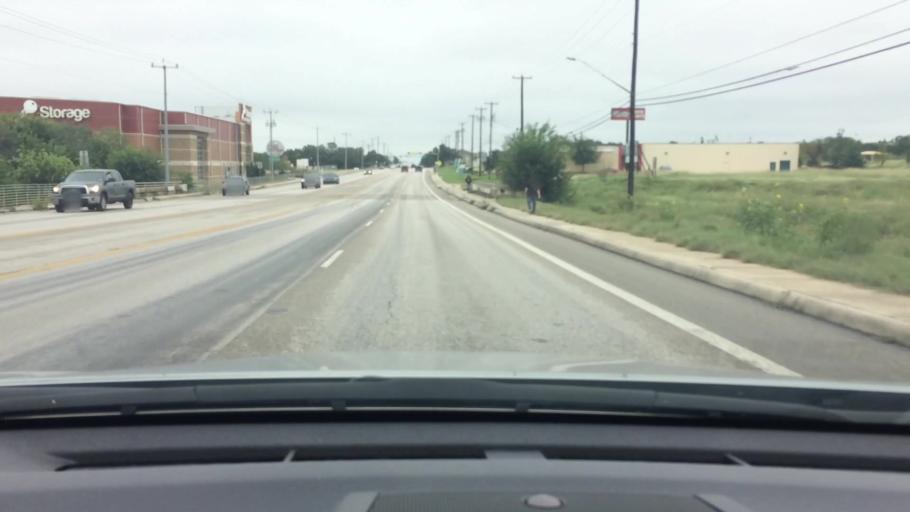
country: US
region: Texas
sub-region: Bexar County
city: Helotes
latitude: 29.5020
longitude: -98.7254
